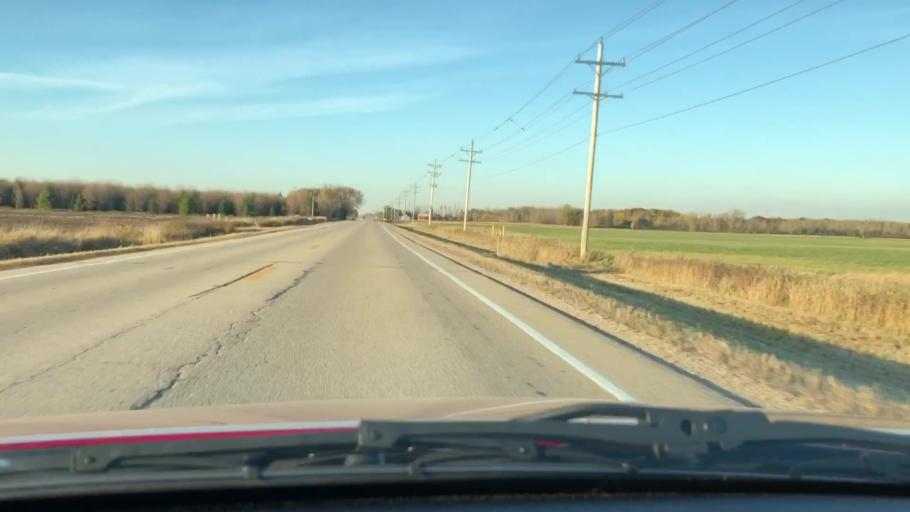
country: US
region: Wisconsin
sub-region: Outagamie County
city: Seymour
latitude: 44.4676
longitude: -88.2911
